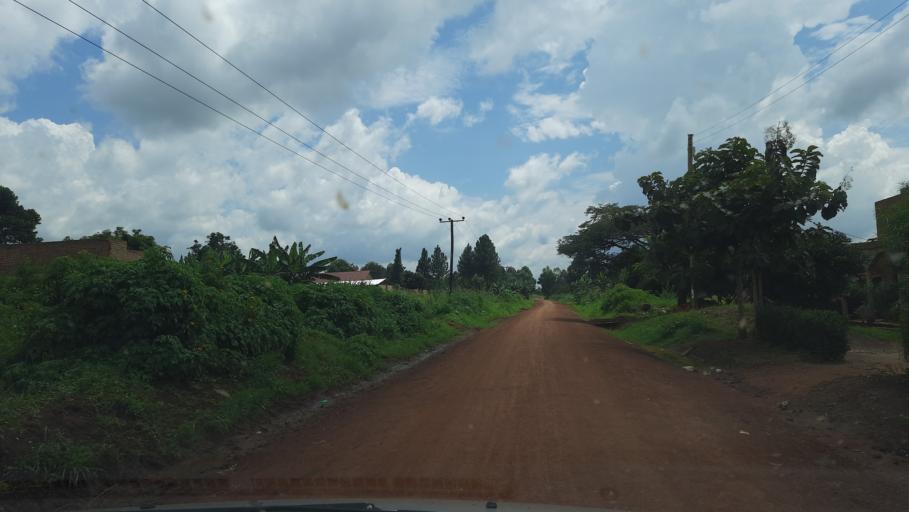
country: UG
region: Western Region
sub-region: Kiryandongo District
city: Kiryandongo
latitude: 1.8131
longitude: 31.9976
